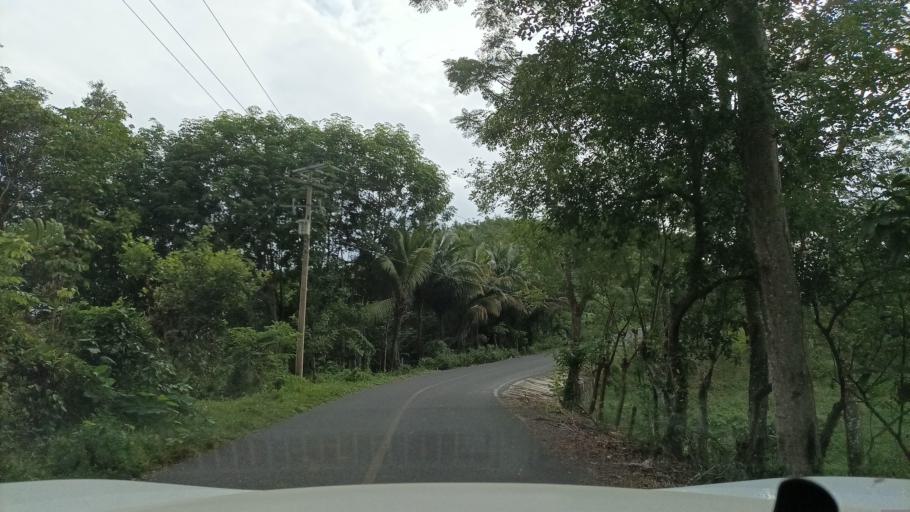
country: MX
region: Veracruz
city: Hidalgotitlan
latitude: 17.6906
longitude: -94.4552
